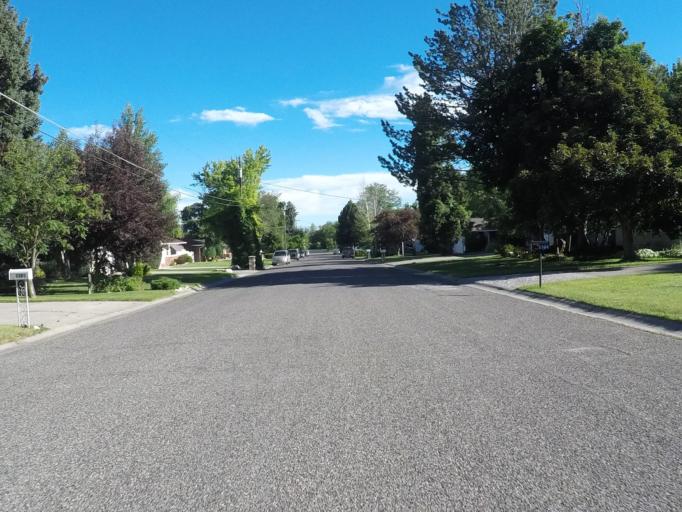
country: US
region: Montana
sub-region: Yellowstone County
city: Billings
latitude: 45.7935
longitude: -108.5846
